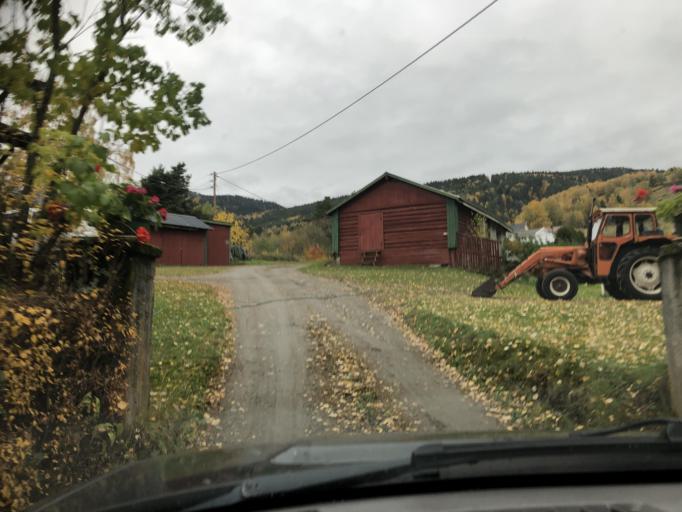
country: NO
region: Oppland
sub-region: Sor-Fron
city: Hundorp
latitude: 61.5736
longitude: 9.9145
